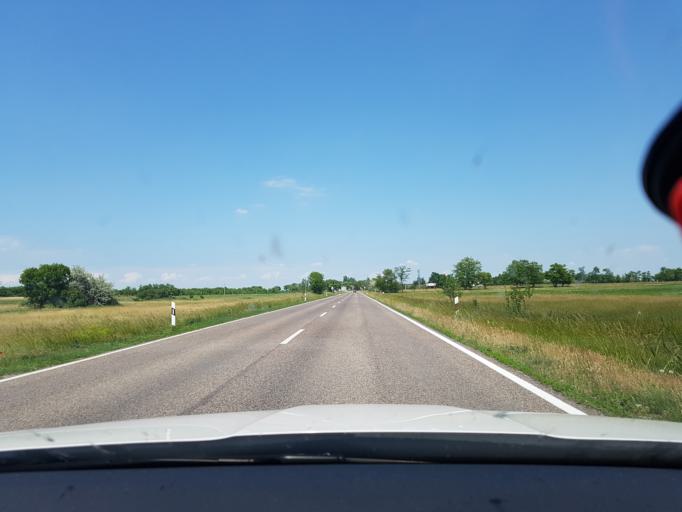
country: HU
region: Hajdu-Bihar
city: Egyek
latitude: 47.5858
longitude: 20.8534
